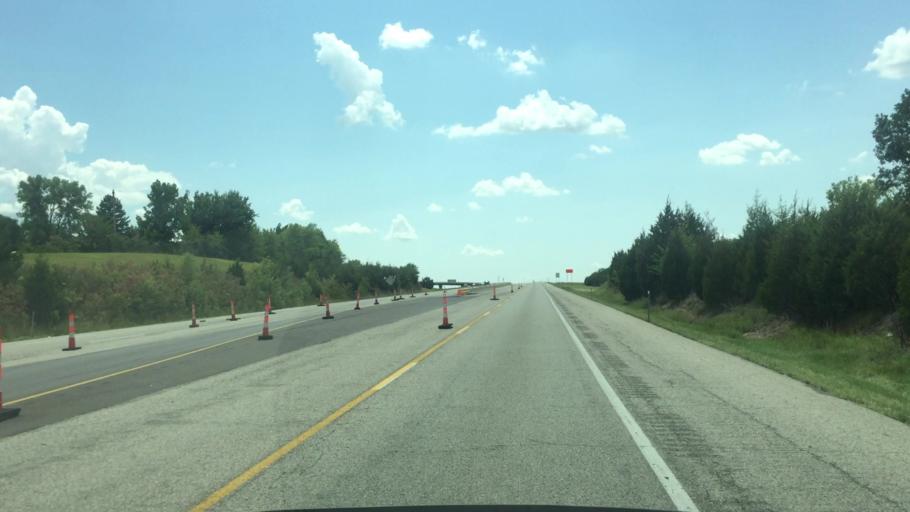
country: US
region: Kansas
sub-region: Lyon County
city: Emporia
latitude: 38.4392
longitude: -96.2185
